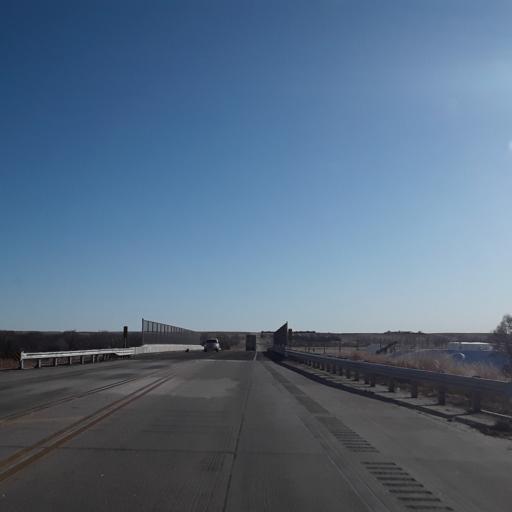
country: US
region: Nebraska
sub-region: Dundy County
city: Benkelman
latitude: 40.0434
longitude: -101.5436
